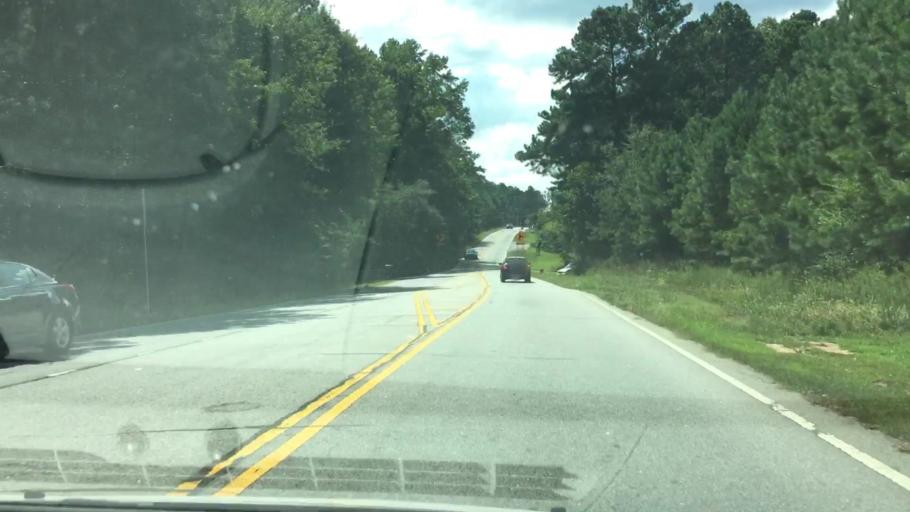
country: US
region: Georgia
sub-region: Clayton County
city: Irondale
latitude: 33.4579
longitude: -84.4034
